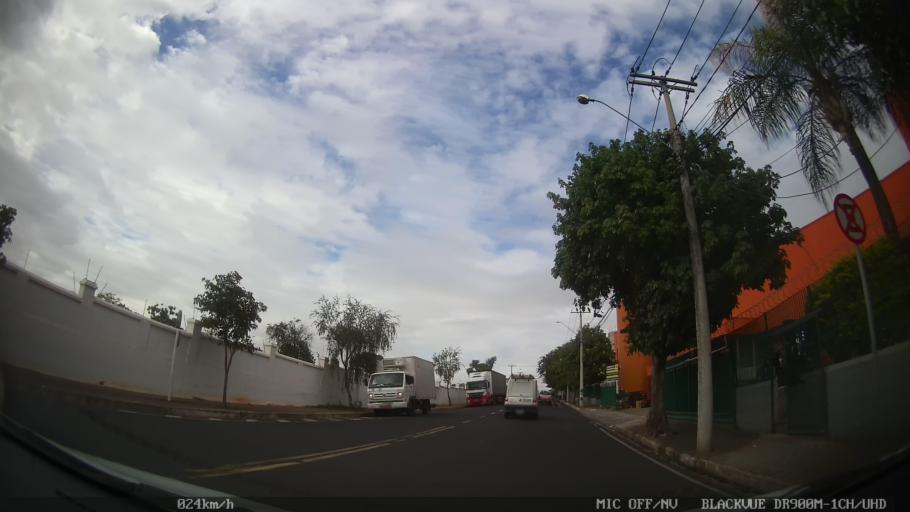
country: BR
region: Sao Paulo
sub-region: Sao Jose Do Rio Preto
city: Sao Jose do Rio Preto
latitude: -20.8182
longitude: -49.3722
